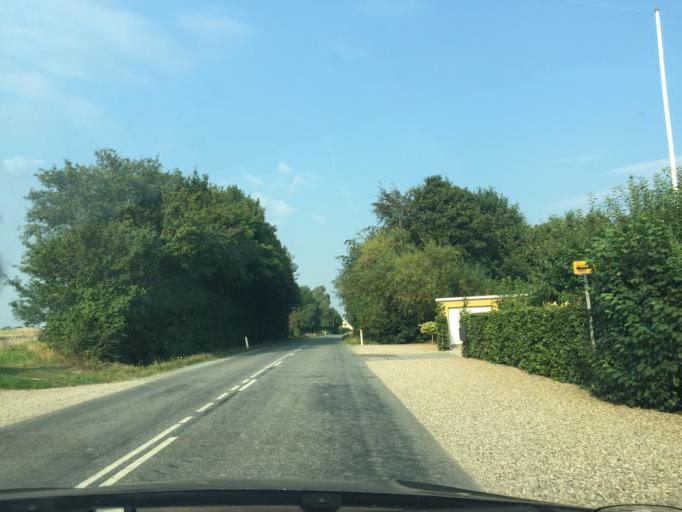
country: DK
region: South Denmark
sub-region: Faaborg-Midtfyn Kommune
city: Arslev
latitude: 55.2829
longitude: 10.4659
